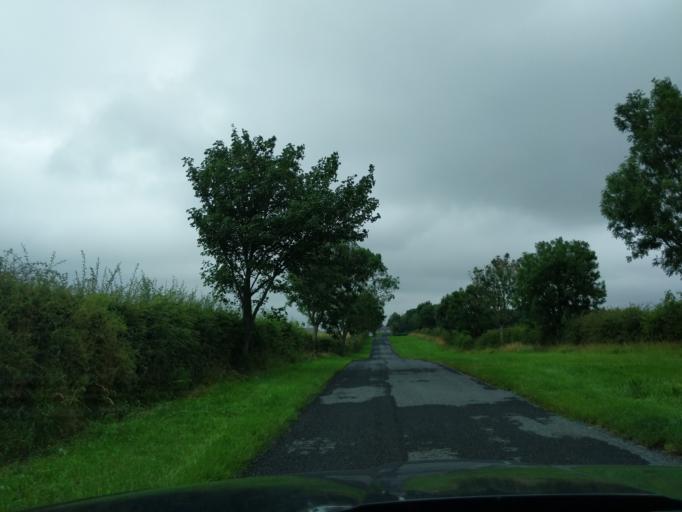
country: GB
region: England
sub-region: Northumberland
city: Ford
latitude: 55.6935
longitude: -2.1339
